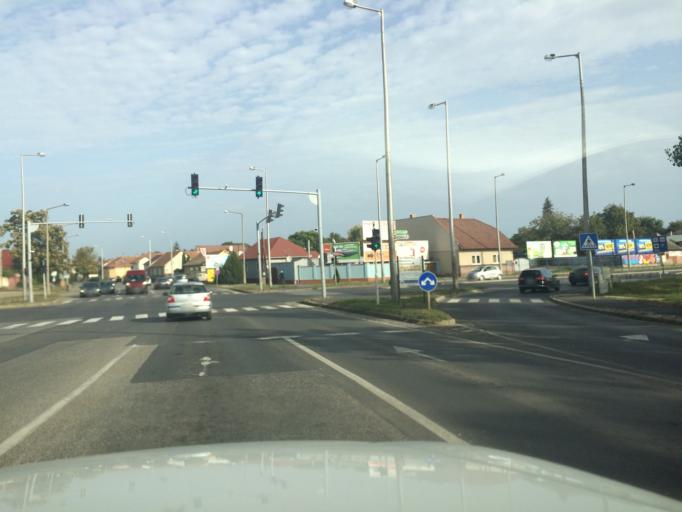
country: HU
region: Szabolcs-Szatmar-Bereg
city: Nyiregyhaza
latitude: 47.9422
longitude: 21.7200
